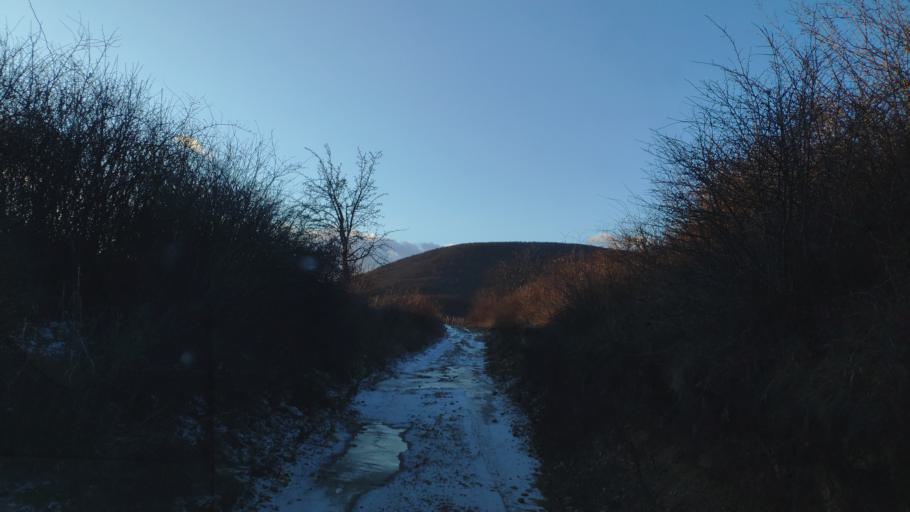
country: HU
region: Borsod-Abauj-Zemplen
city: Olaszliszka
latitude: 48.2747
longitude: 21.4030
